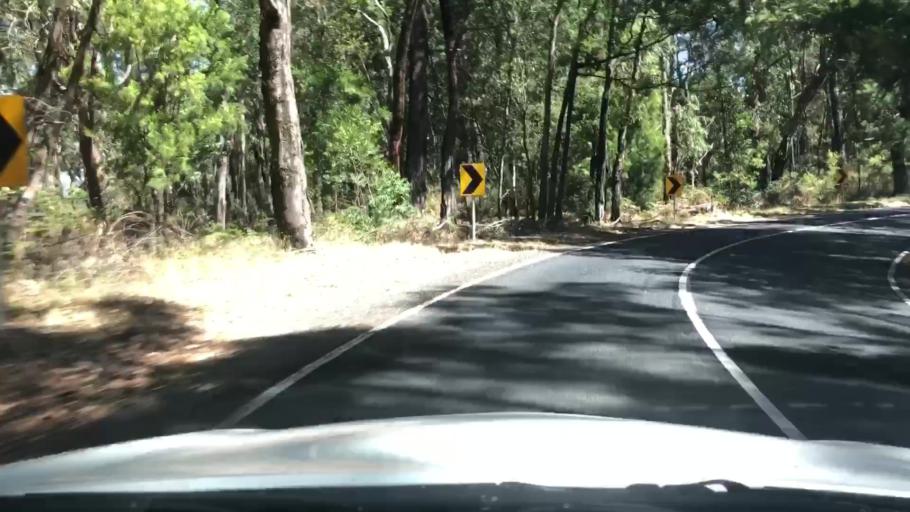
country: AU
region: Victoria
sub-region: Yarra Ranges
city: Macclesfield
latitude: -37.8370
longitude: 145.4888
